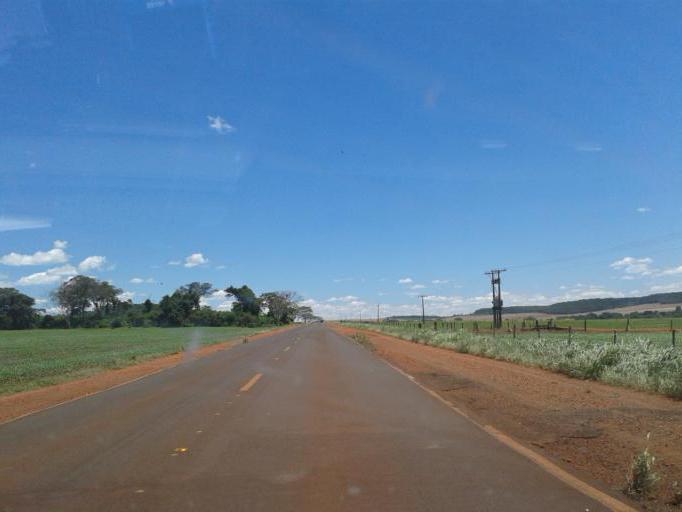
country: BR
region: Minas Gerais
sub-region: Capinopolis
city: Capinopolis
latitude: -18.6022
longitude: -49.5231
